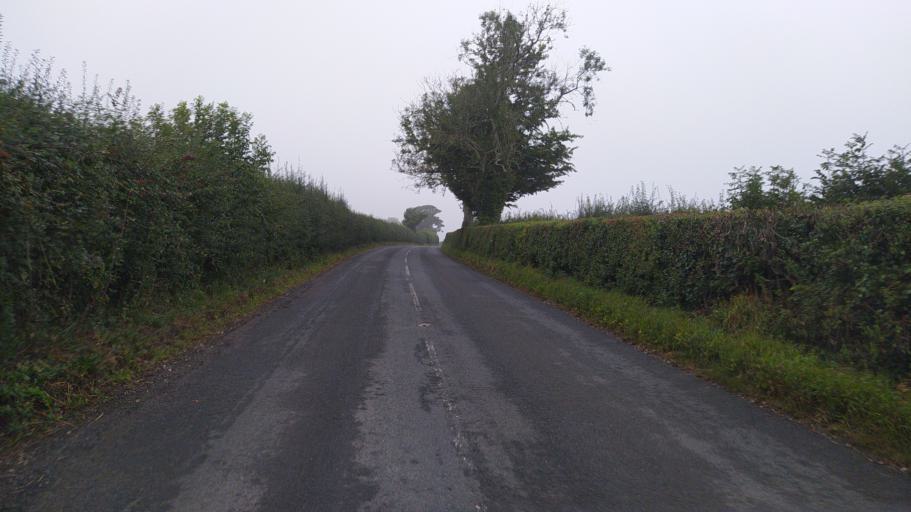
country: GB
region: England
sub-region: Wiltshire
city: Ansty
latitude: 50.9616
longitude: -2.1052
